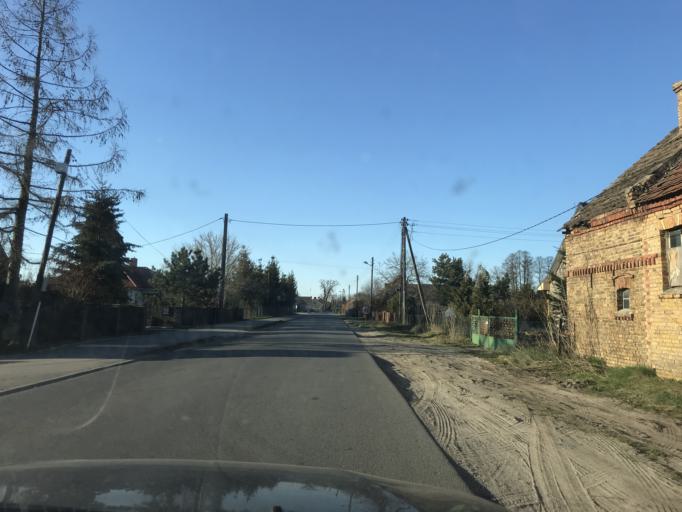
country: PL
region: Lubusz
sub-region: Powiat gorzowski
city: Deszczno
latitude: 52.6585
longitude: 15.3133
